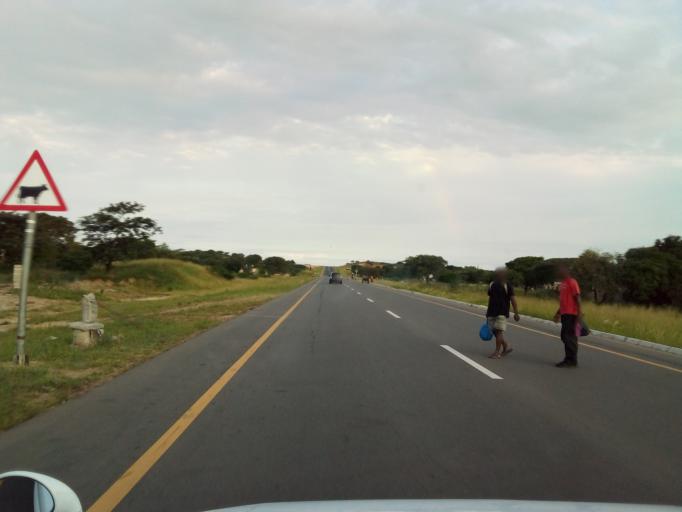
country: MZ
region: Maputo City
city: Maputo
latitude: -26.0399
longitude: 32.5618
